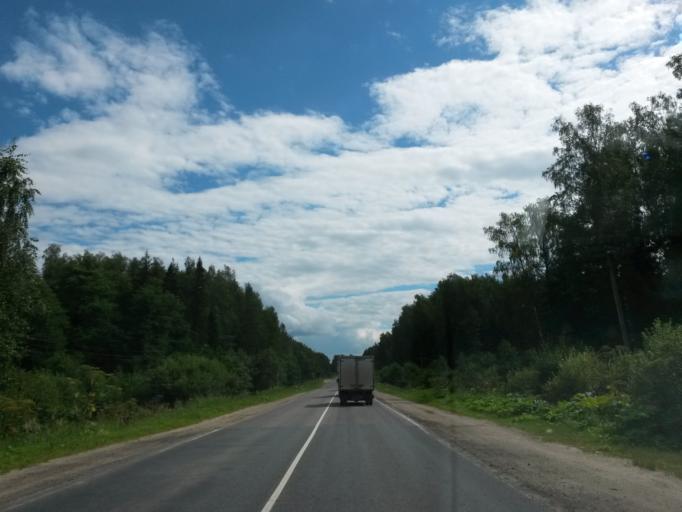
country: RU
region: Ivanovo
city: Novo-Talitsy
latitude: 57.0583
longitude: 40.7245
